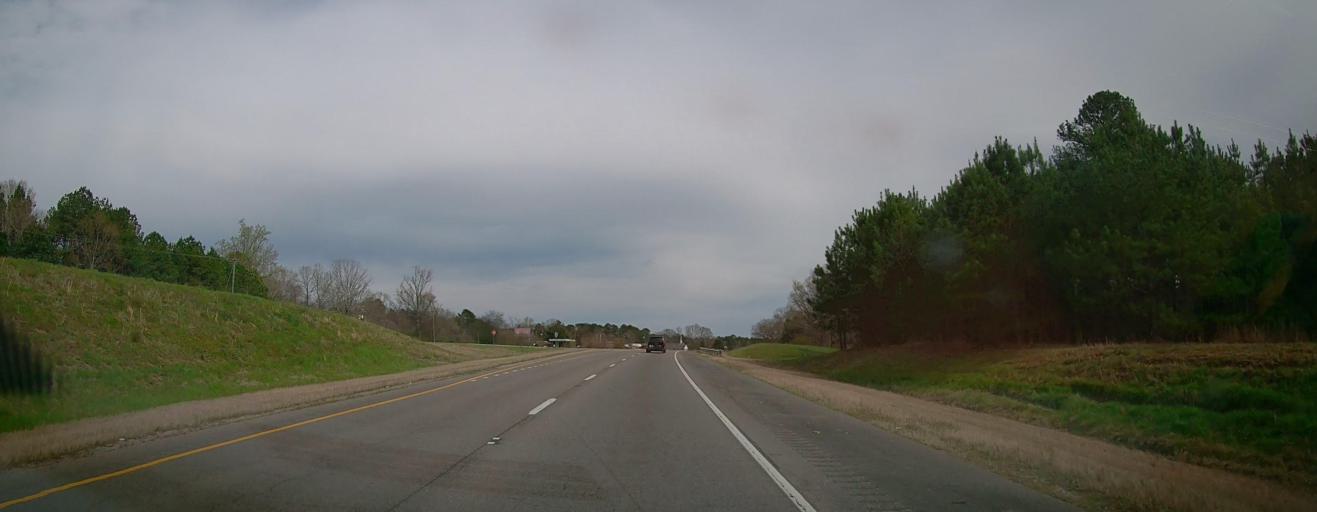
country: US
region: Alabama
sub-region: Walker County
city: Cordova
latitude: 33.8026
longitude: -87.1216
